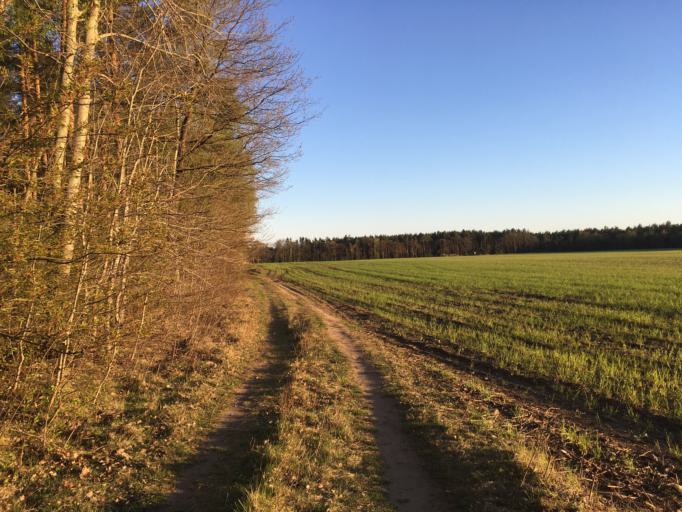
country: DE
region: Lower Saxony
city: Wendisch Evern
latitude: 53.2264
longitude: 10.4426
